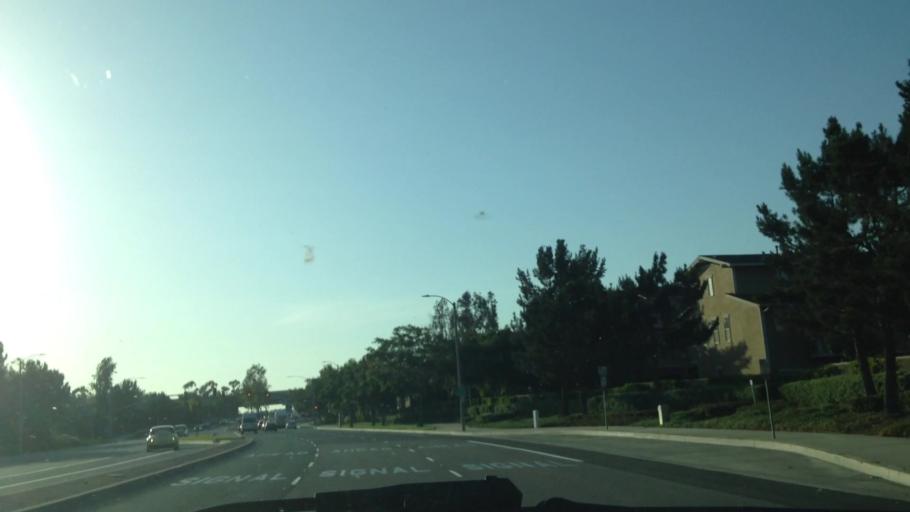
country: US
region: California
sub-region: Orange County
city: Irvine
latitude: 33.7013
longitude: -117.8027
